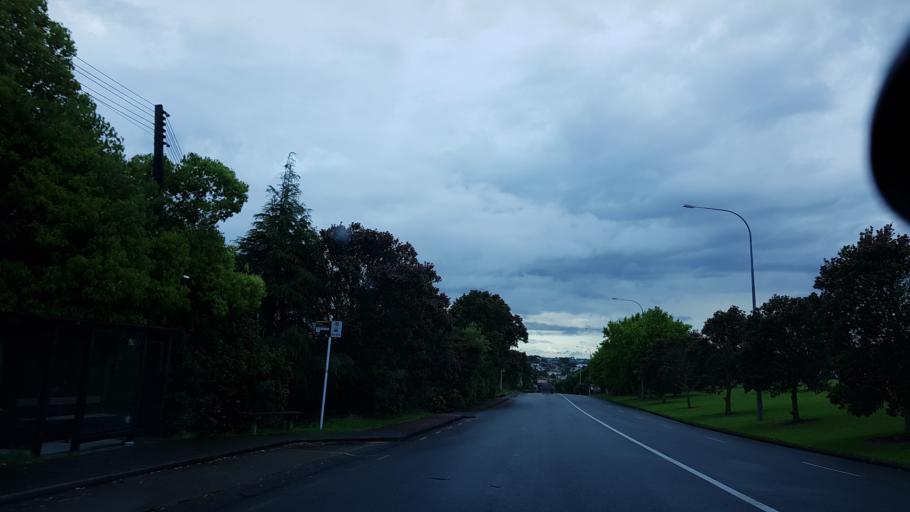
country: NZ
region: Auckland
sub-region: Auckland
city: North Shore
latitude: -36.7876
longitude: 174.7214
